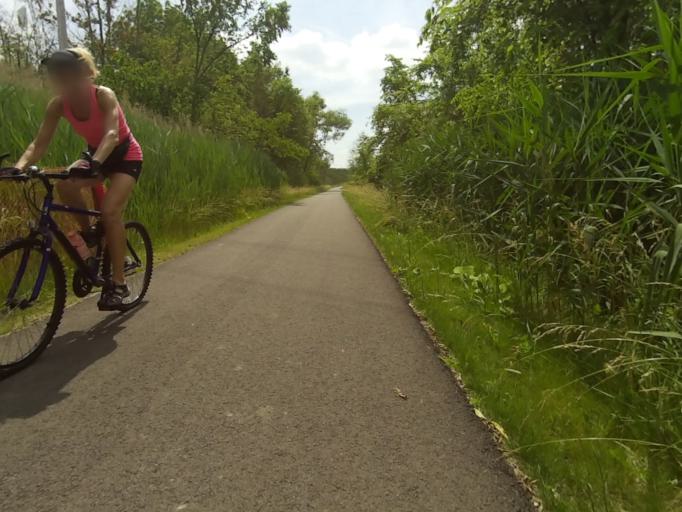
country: US
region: Ohio
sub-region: Summit County
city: Boston Heights
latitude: 41.2320
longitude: -81.4942
